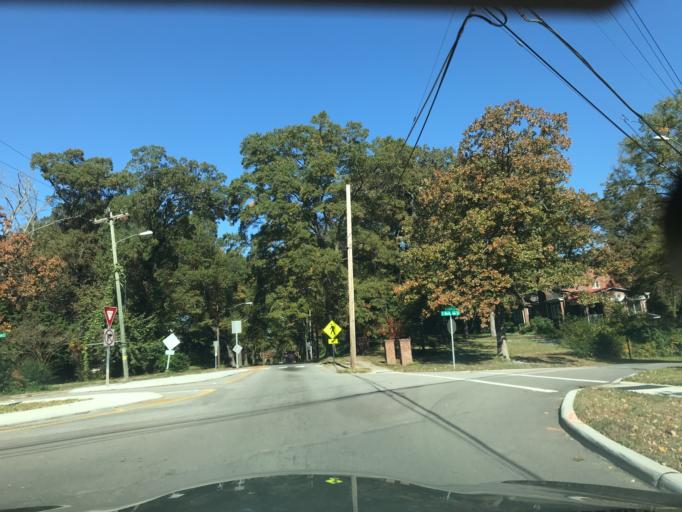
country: US
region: North Carolina
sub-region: Durham County
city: Durham
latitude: 36.0098
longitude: -78.8918
